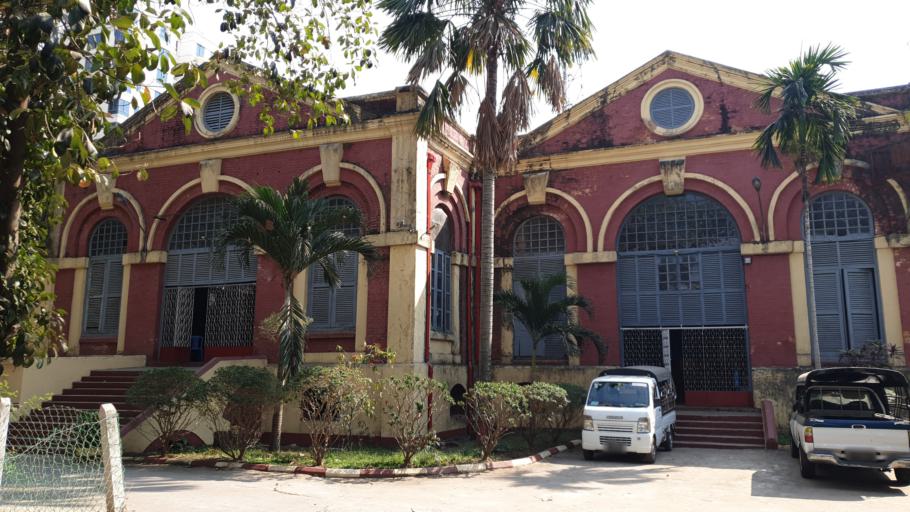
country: MM
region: Yangon
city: Yangon
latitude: 16.7736
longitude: 96.1688
